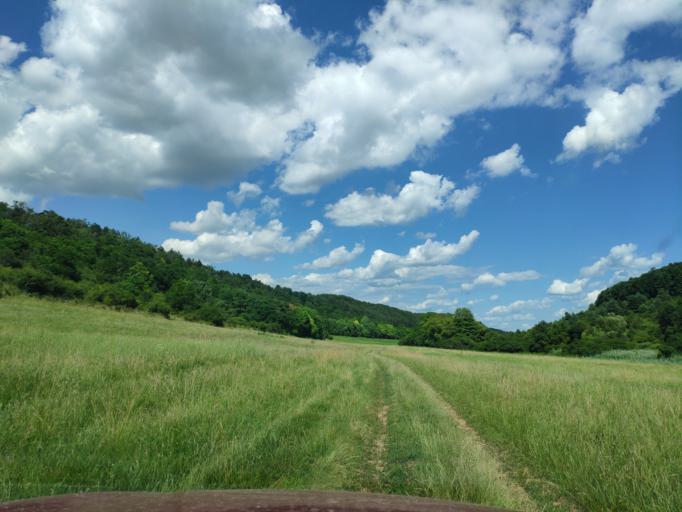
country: HU
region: Borsod-Abauj-Zemplen
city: Arlo
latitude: 48.2665
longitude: 20.1812
